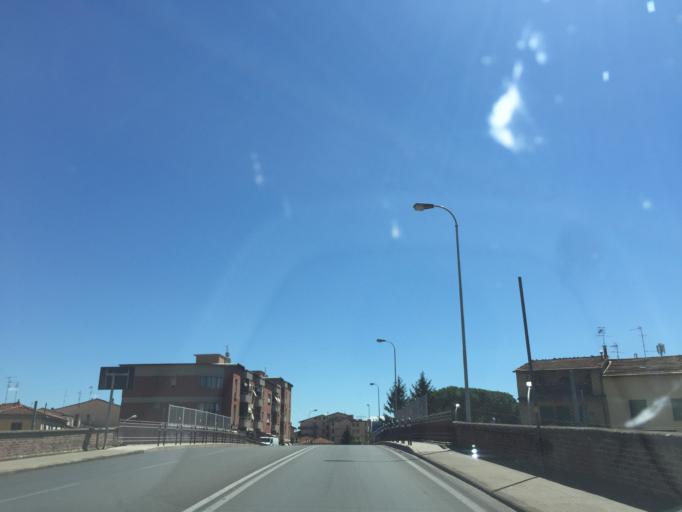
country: IT
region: Tuscany
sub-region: Provincia di Pistoia
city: Pistoia
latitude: 43.9276
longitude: 10.9189
